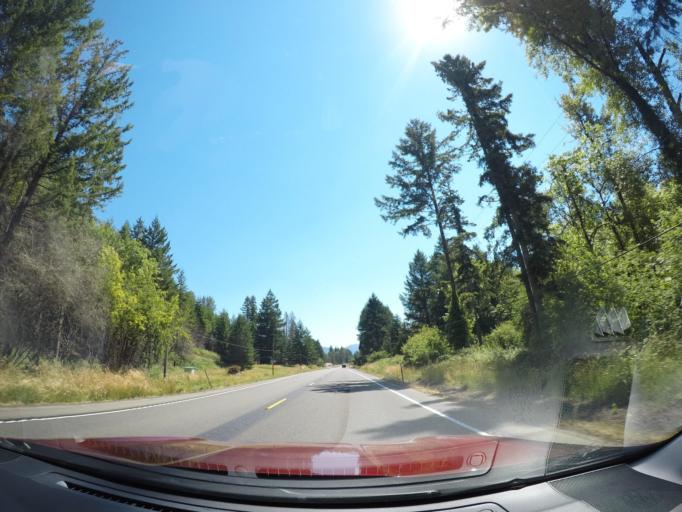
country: US
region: Oregon
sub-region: Linn County
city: Mill City
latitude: 44.7569
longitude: -122.4430
